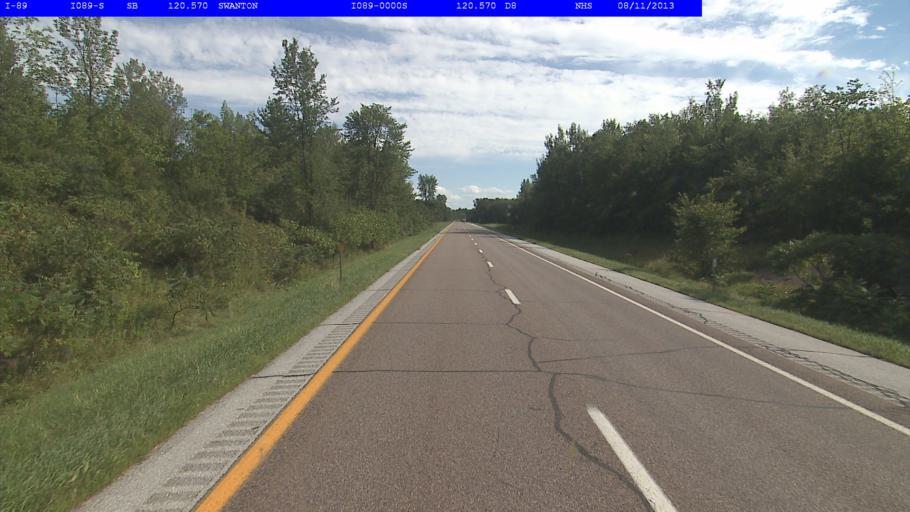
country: US
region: Vermont
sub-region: Franklin County
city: Swanton
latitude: 44.8850
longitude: -73.0858
